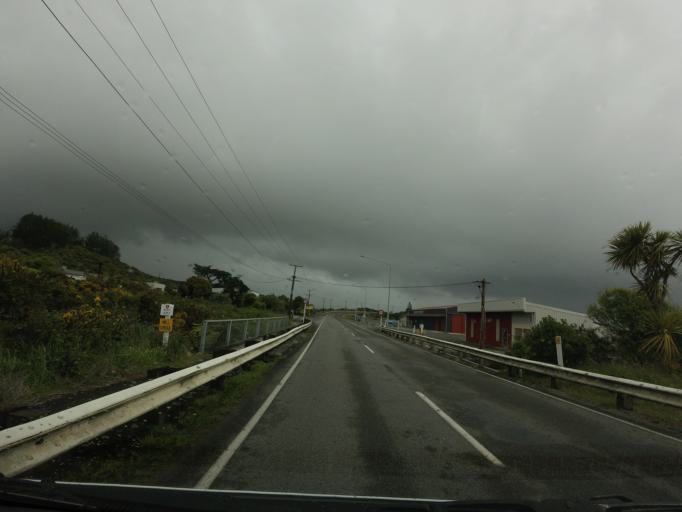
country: NZ
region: West Coast
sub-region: Grey District
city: Greymouth
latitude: -42.4884
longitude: 171.1802
